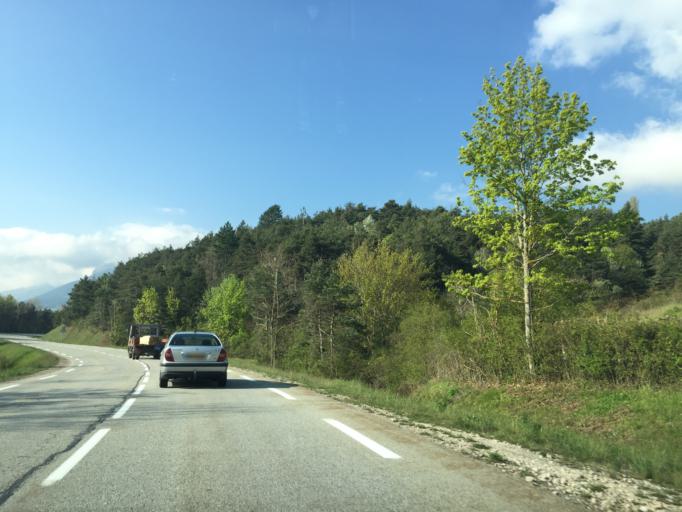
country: FR
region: Rhone-Alpes
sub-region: Departement de l'Isere
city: Mens
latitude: 44.8480
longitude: 5.6186
